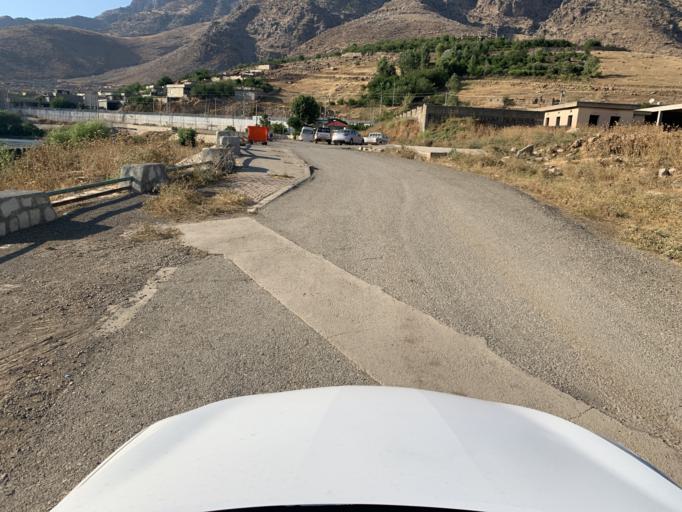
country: IQ
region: As Sulaymaniyah
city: Raniye
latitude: 36.2740
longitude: 44.7562
